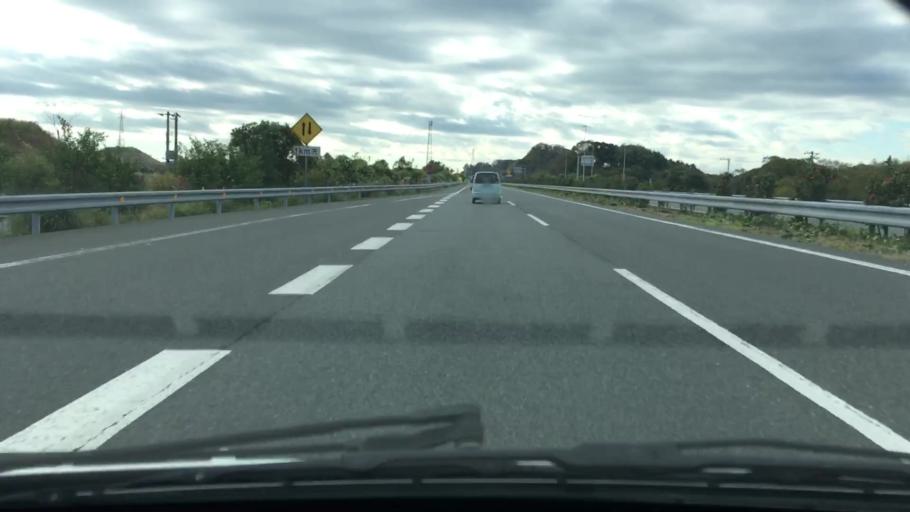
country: JP
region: Chiba
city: Kimitsu
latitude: 35.2510
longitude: 139.8919
